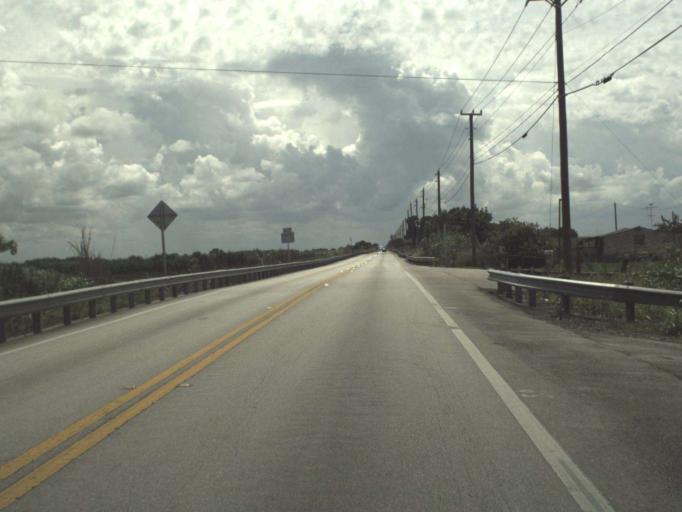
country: US
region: Florida
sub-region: Palm Beach County
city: Pahokee
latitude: 26.8060
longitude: -80.6534
